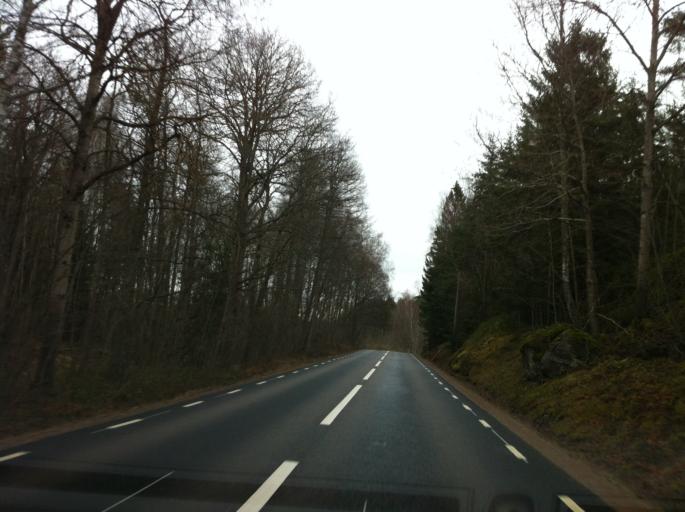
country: SE
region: Kalmar
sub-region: Vasterviks Kommun
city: Overum
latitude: 57.9082
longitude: 16.2036
